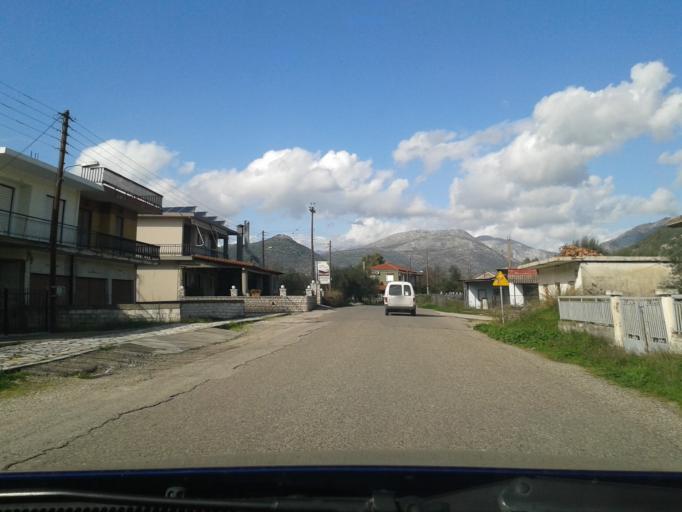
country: GR
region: West Greece
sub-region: Nomos Aitolias kai Akarnanias
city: Astakos
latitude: 38.5782
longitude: 21.0907
